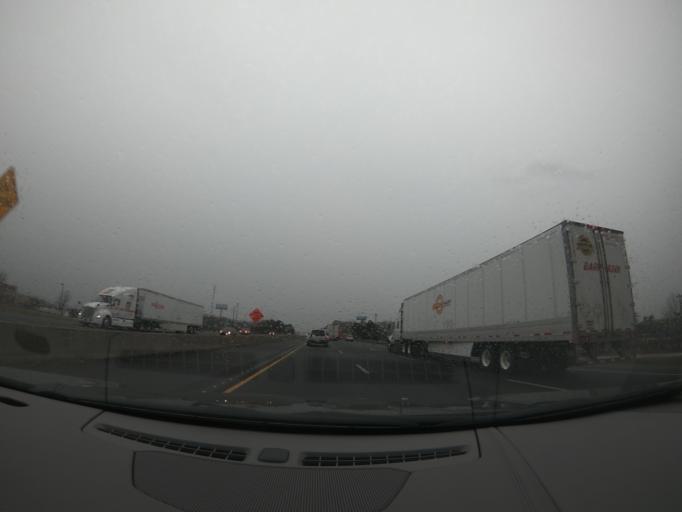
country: US
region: Georgia
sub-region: Catoosa County
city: Indian Springs
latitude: 34.9295
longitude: -85.1533
